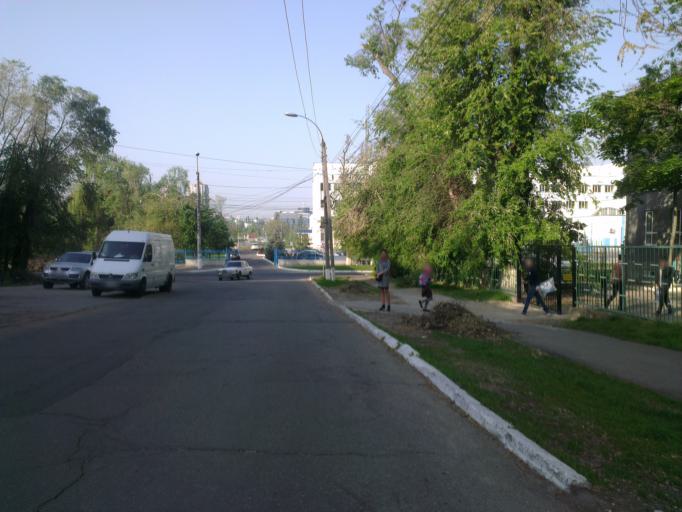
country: MD
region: Chisinau
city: Chisinau
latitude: 47.0358
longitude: 28.8552
